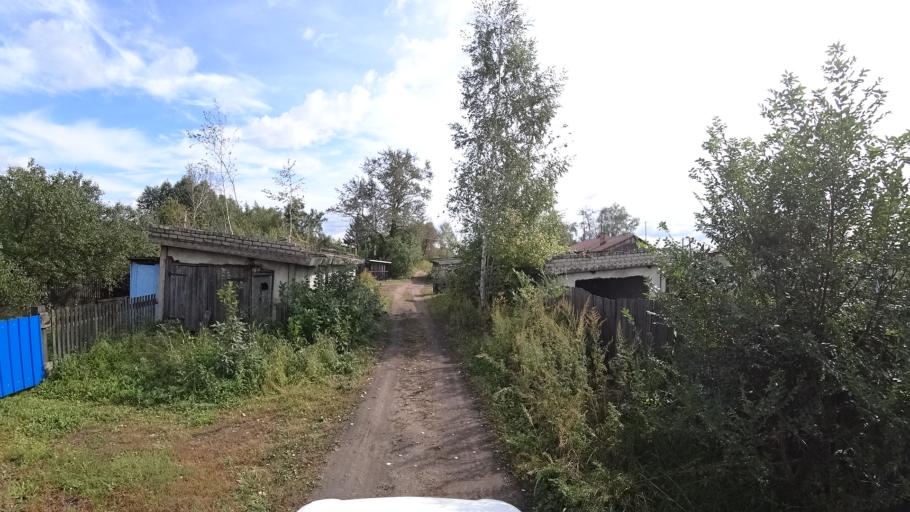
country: RU
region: Amur
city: Arkhara
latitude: 49.3531
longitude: 130.1589
